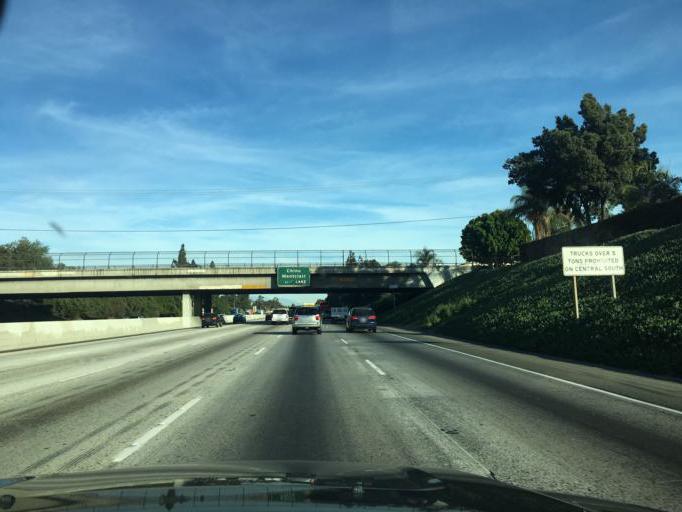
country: US
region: California
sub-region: San Bernardino County
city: Chino
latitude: 34.0300
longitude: -117.6991
